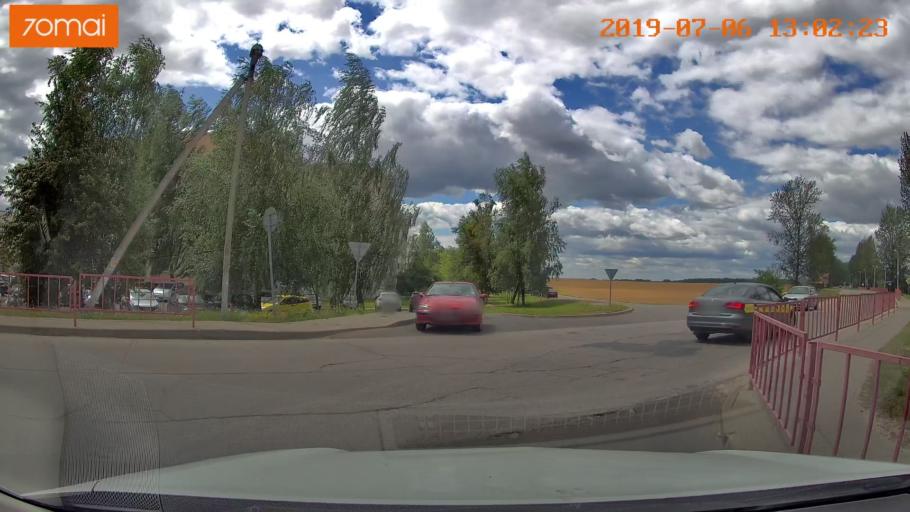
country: BY
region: Minsk
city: Dzyarzhynsk
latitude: 53.6868
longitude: 27.1161
